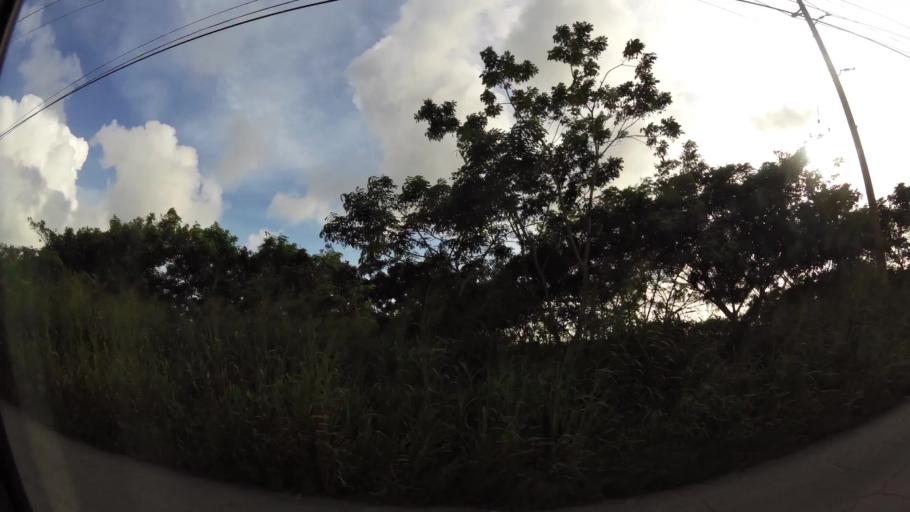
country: BB
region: Christ Church
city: Oistins
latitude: 13.0941
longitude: -59.5537
